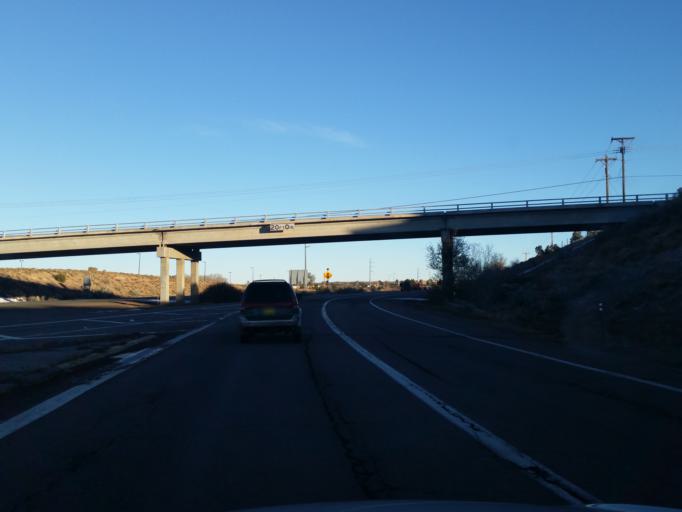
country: US
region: New Mexico
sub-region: Santa Fe County
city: Santa Fe
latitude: 35.6379
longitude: -105.9560
